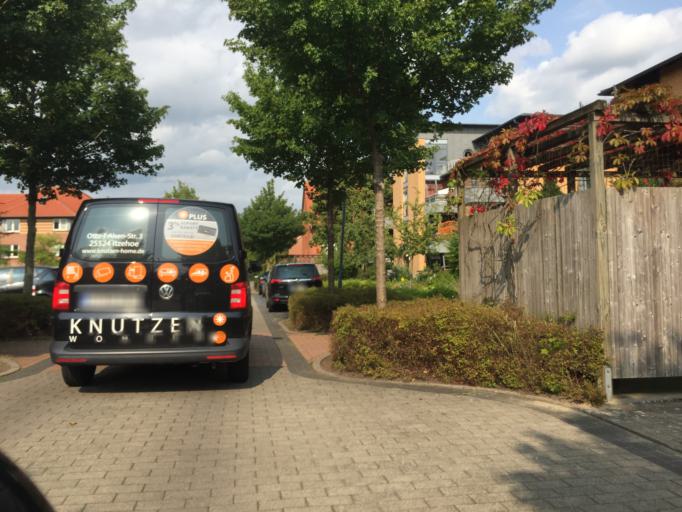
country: DE
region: Schleswig-Holstein
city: Itzehoe
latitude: 53.9326
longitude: 9.5223
